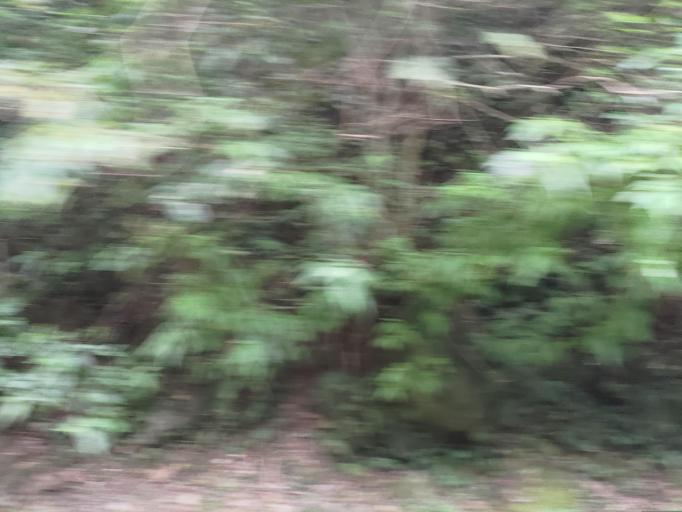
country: TW
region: Taiwan
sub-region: Hsinchu
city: Hsinchu
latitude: 24.6043
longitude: 121.0388
